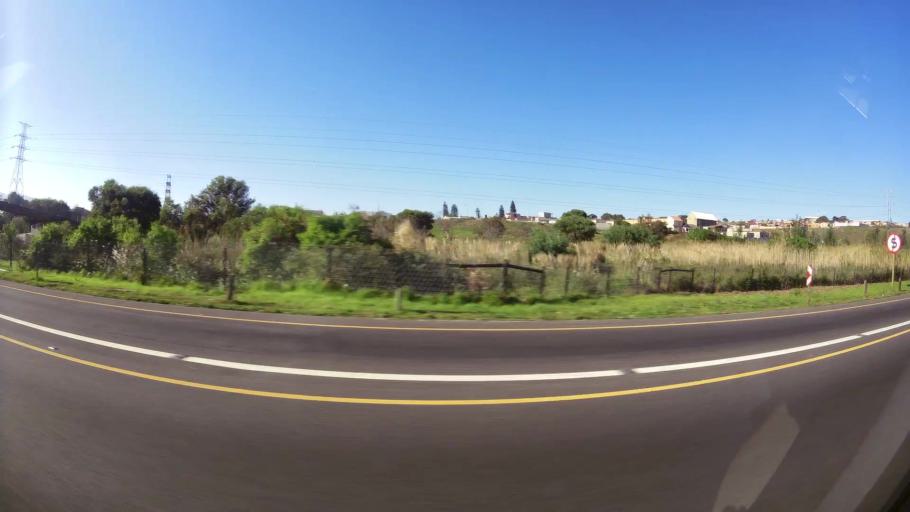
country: ZA
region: Eastern Cape
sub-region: Nelson Mandela Bay Metropolitan Municipality
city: Port Elizabeth
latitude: -33.9247
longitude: 25.5627
